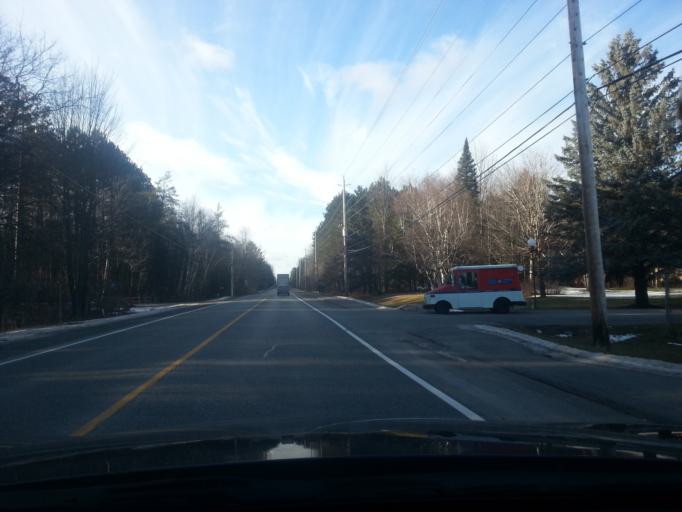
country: CA
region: Ontario
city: Ottawa
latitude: 45.3230
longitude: -75.7269
